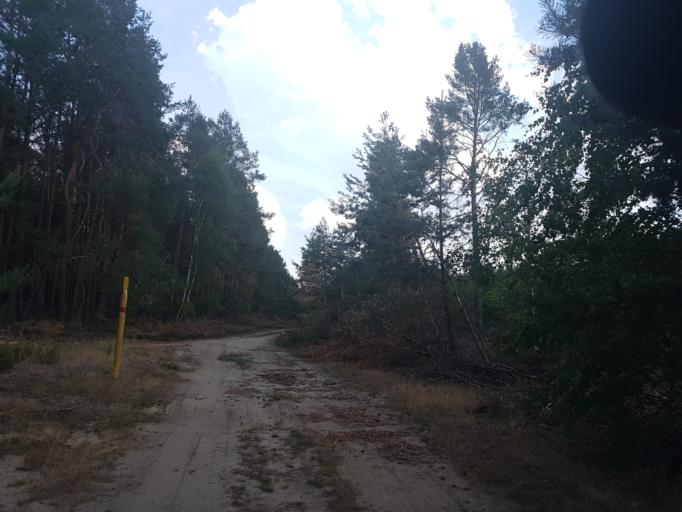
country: DE
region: Brandenburg
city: Treuenbrietzen
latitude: 52.0516
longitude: 12.8446
